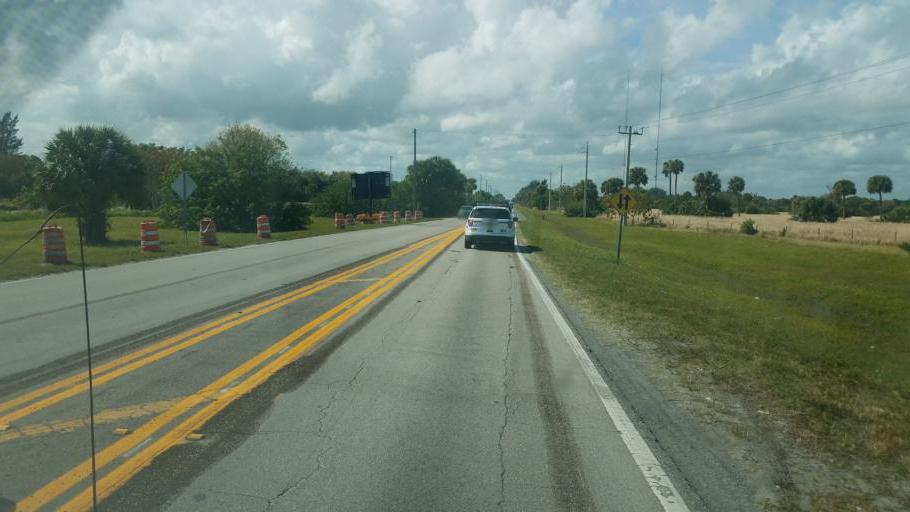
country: US
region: Florida
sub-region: Saint Lucie County
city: Lakewood Park
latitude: 27.4475
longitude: -80.4009
